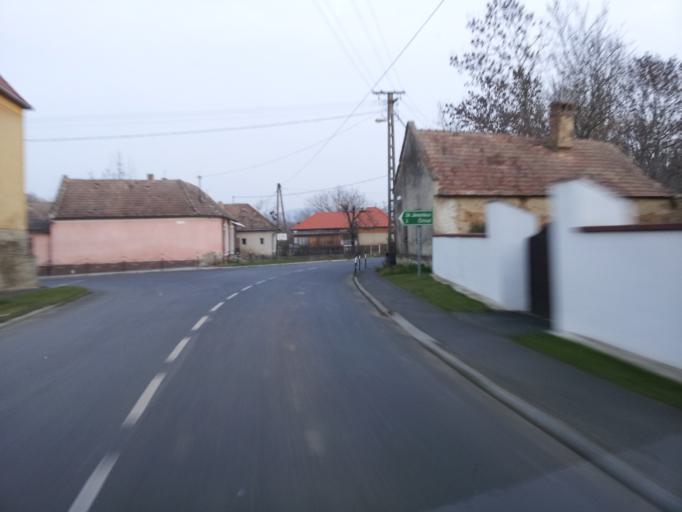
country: HU
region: Zala
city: Turje
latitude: 46.9363
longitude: 17.1572
